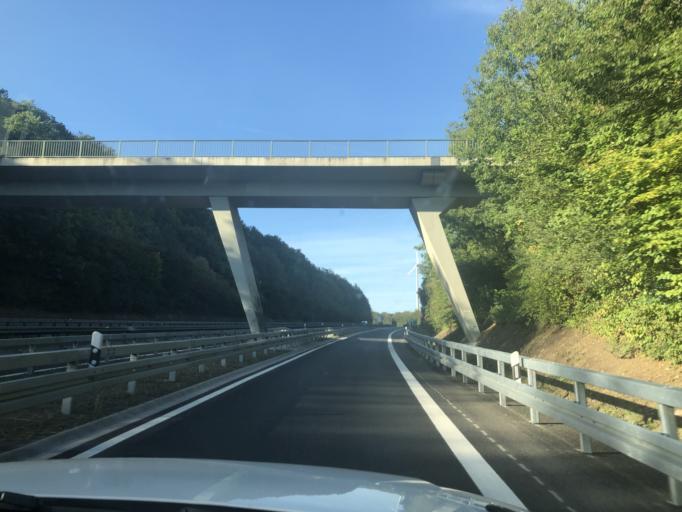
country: DE
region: Saarland
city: Eppelborn
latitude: 49.4246
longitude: 6.9712
